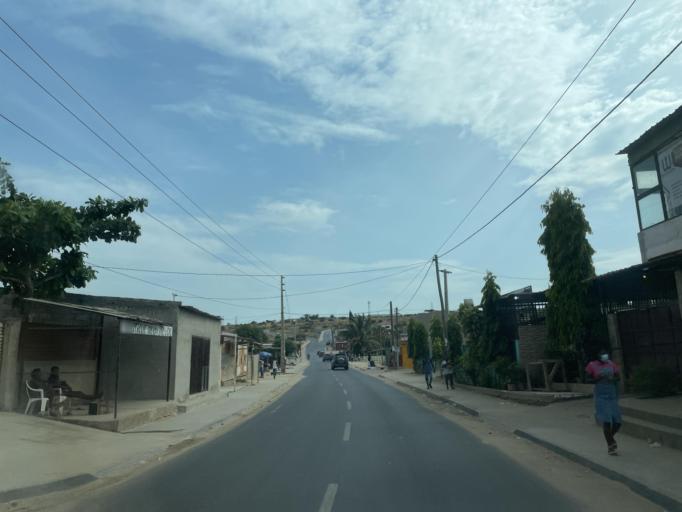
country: AO
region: Luanda
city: Luanda
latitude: -8.9359
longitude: 13.1970
